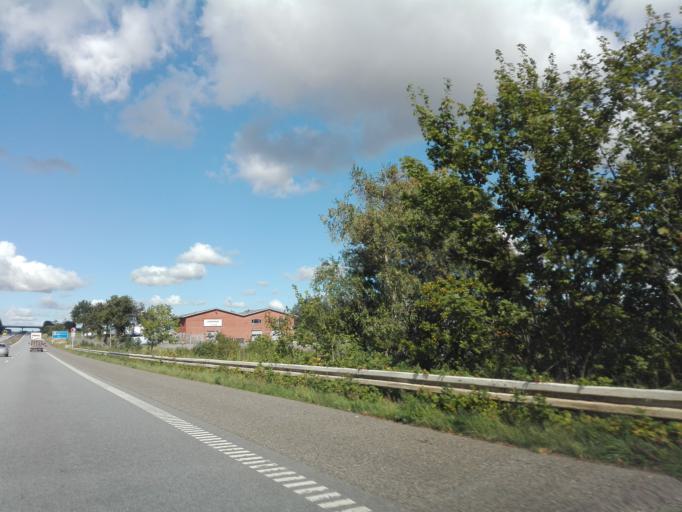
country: DK
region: Central Jutland
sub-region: Randers Kommune
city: Randers
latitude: 56.4796
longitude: 9.9814
